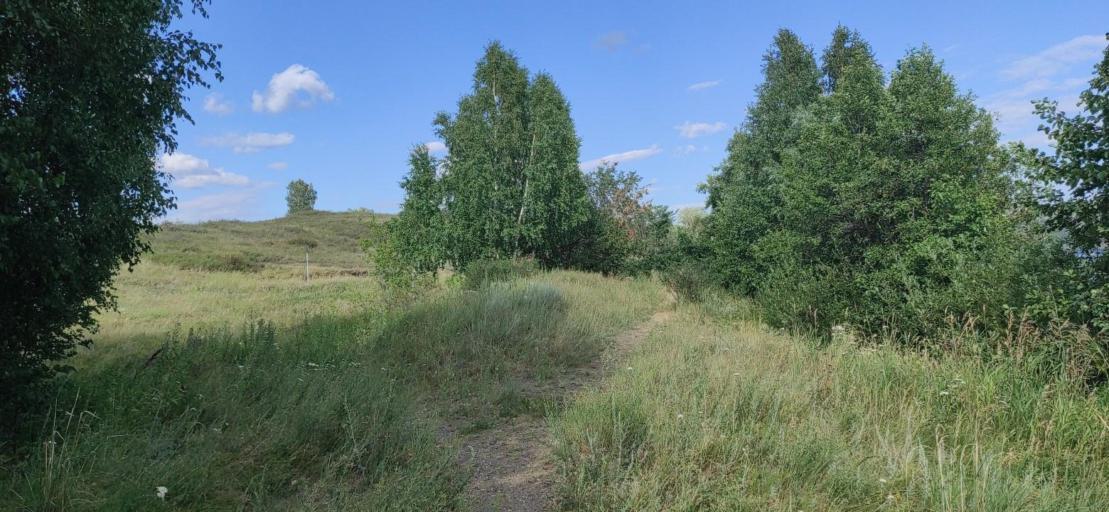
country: RU
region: Bashkortostan
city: Abzakovo
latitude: 53.5969
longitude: 58.6098
